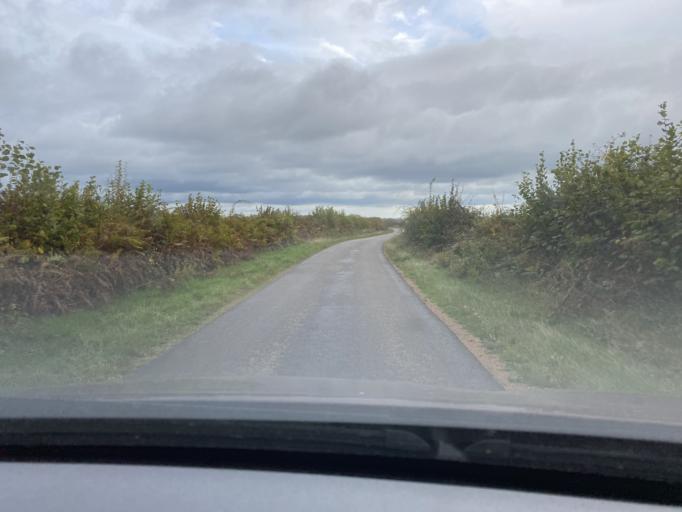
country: FR
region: Bourgogne
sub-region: Departement de la Cote-d'Or
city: Saulieu
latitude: 47.2848
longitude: 4.2194
